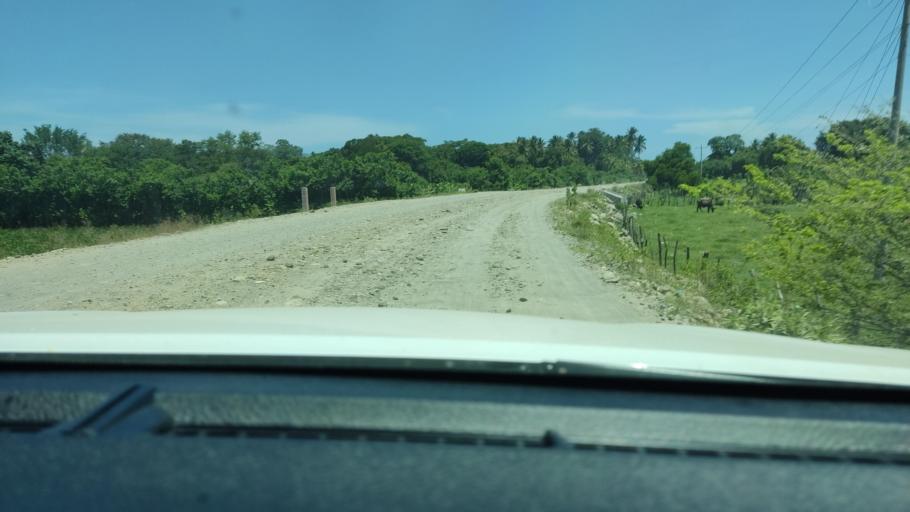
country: SV
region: Ahuachapan
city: San Francisco Menendez
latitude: 13.7934
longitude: -90.1171
